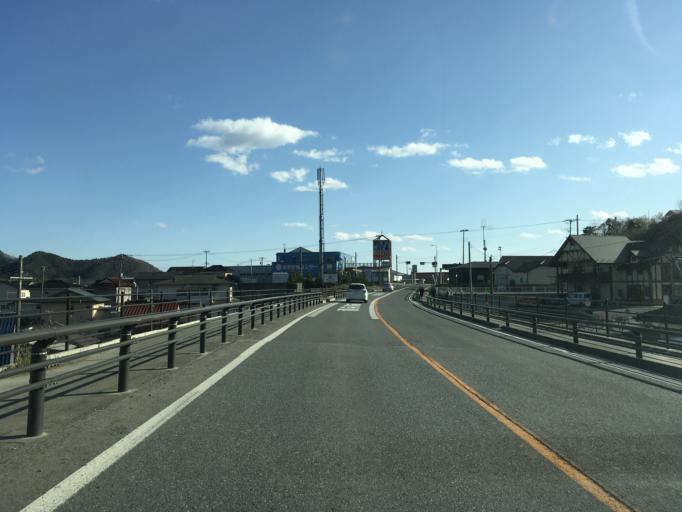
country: JP
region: Iwate
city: Ofunato
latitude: 39.0438
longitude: 141.7220
